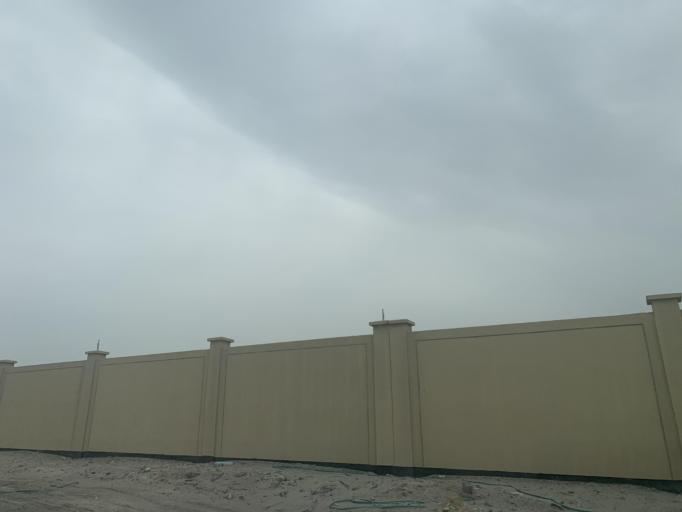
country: BH
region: Muharraq
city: Al Hadd
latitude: 26.2095
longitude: 50.6677
